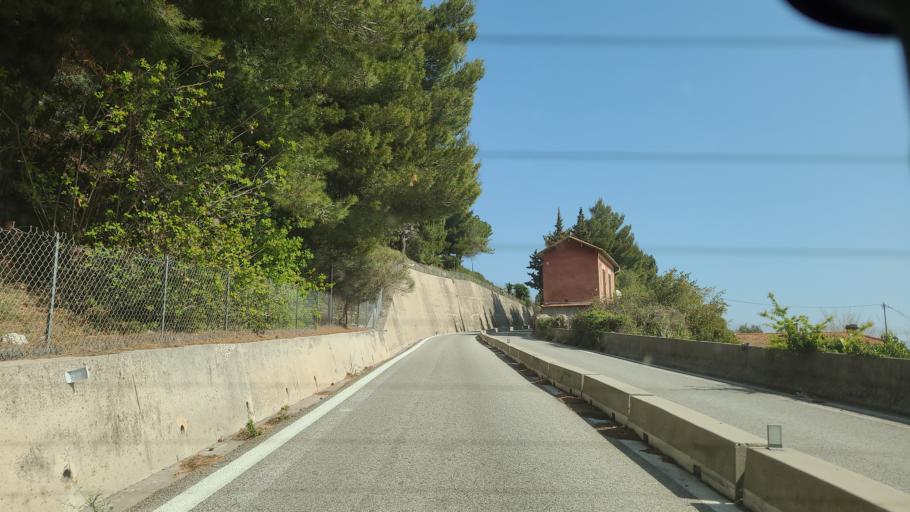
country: MC
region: Commune de Monaco
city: Saint-Roman
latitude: 43.7589
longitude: 7.4442
